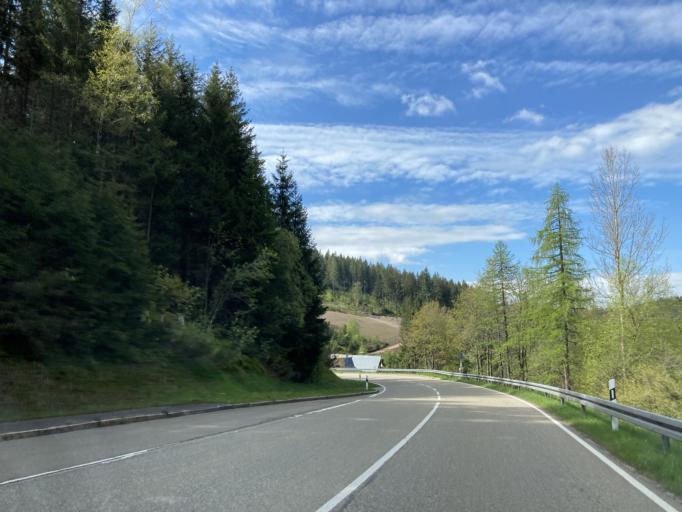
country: DE
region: Baden-Wuerttemberg
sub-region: Freiburg Region
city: Schonwald im Schwarzwald
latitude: 48.0818
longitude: 8.2103
